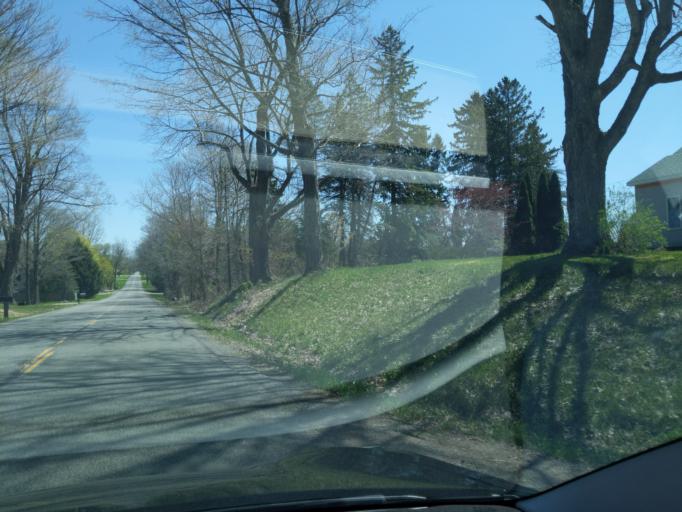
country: US
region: Michigan
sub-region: Ingham County
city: Holt
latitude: 42.5531
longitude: -84.5424
